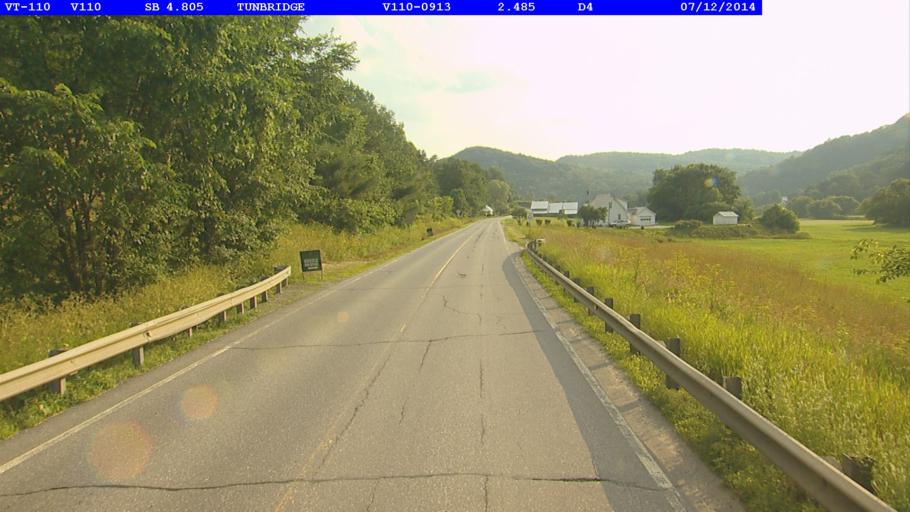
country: US
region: Vermont
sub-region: Orange County
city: Chelsea
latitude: 43.8843
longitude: -72.4965
